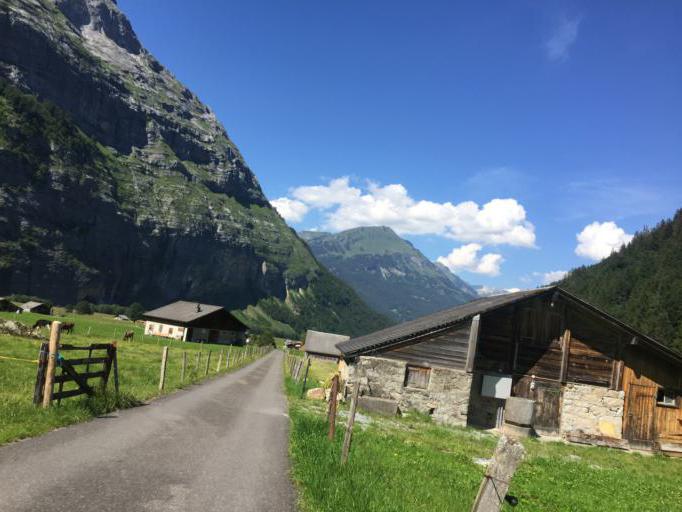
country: CH
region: Bern
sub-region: Interlaken-Oberhasli District
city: Meiringen
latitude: 46.6755
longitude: 8.2072
